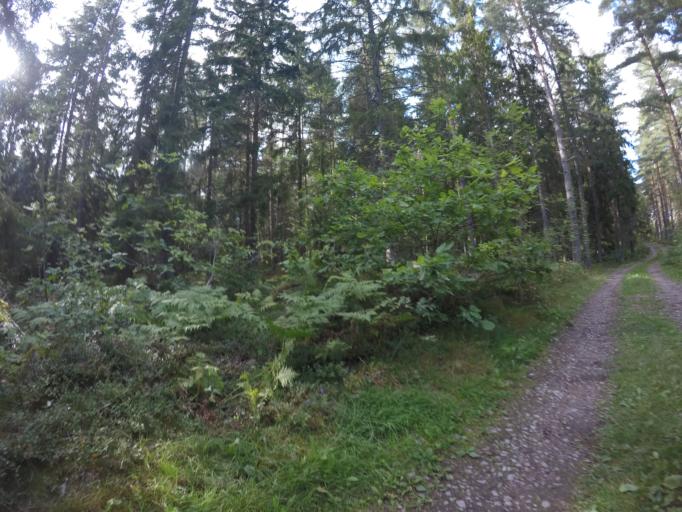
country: SE
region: Soedermanland
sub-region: Eskilstuna Kommun
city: Kvicksund
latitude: 59.5264
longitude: 16.3350
